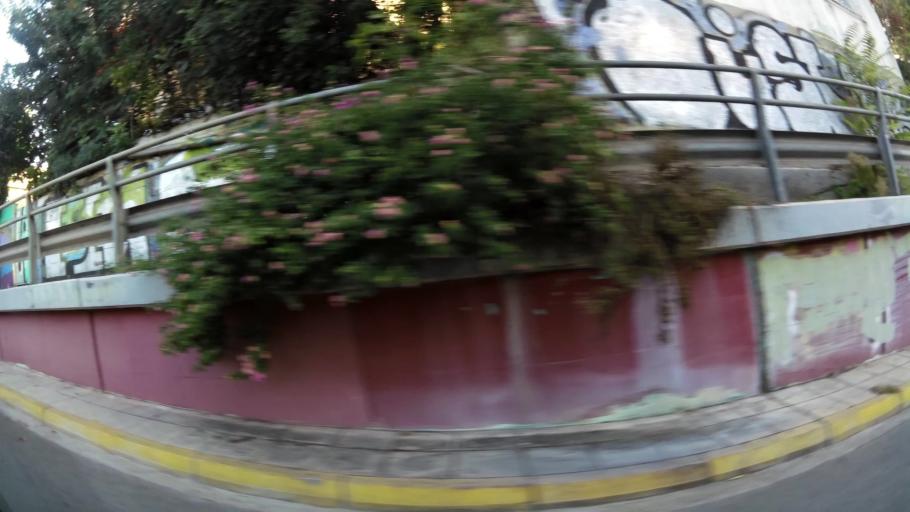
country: GR
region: Attica
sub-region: Nomarchia Athinas
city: Marousi
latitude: 38.0499
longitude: 23.7955
